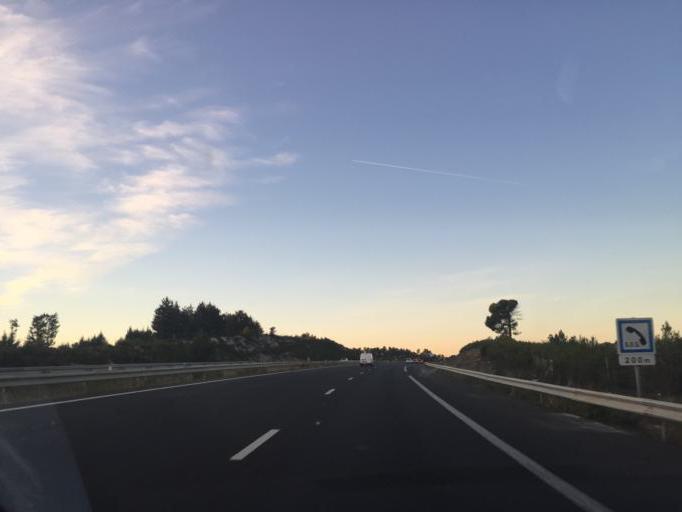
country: FR
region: Provence-Alpes-Cote d'Azur
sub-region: Departement des Bouches-du-Rhone
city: La Fare-les-Oliviers
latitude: 43.5276
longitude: 5.2204
